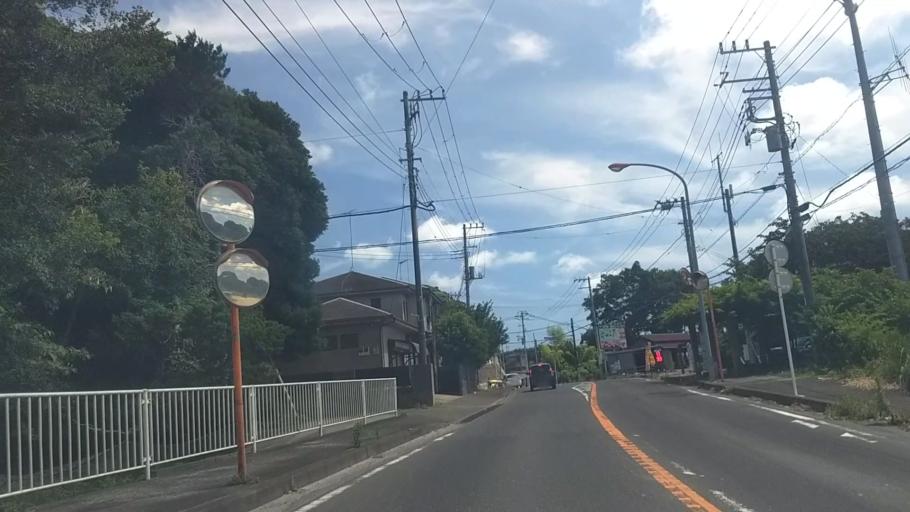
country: JP
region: Kanagawa
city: Miura
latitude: 35.2030
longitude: 139.6492
